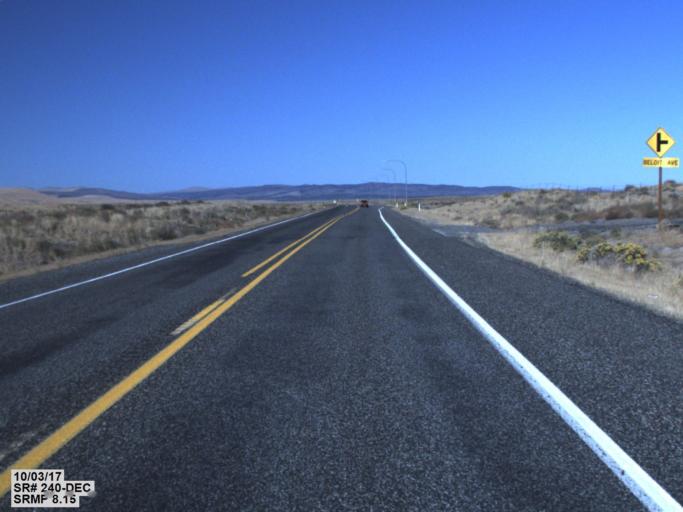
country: US
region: Washington
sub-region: Benton County
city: Benton City
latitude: 46.5007
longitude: -119.6131
